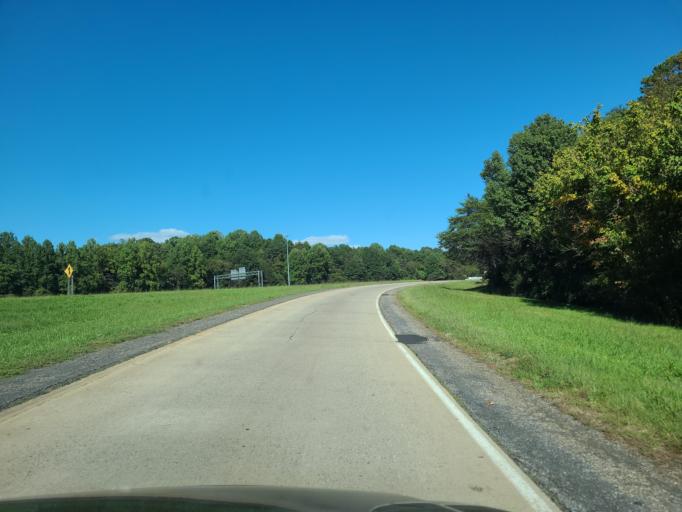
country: US
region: North Carolina
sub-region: Catawba County
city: Hickory
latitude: 35.7077
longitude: -81.3499
